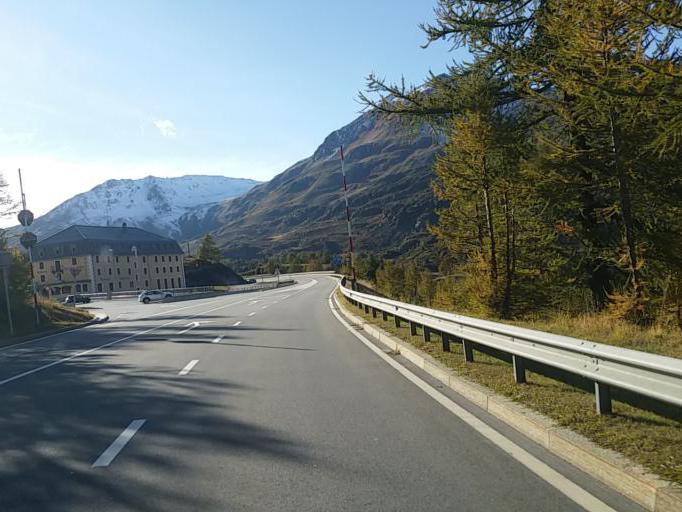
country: CH
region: Valais
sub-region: Brig District
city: Brig
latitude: 46.2510
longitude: 8.0369
